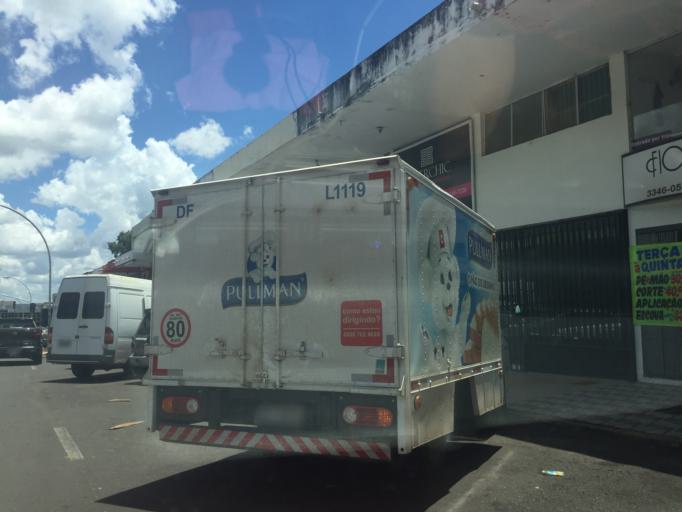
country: BR
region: Federal District
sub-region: Brasilia
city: Brasilia
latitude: -15.8263
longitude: -47.9069
